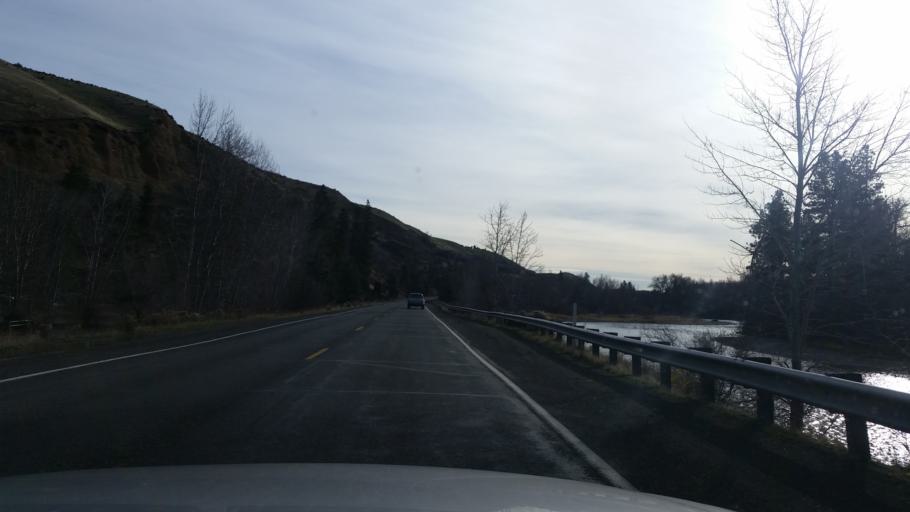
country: US
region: Washington
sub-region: Kittitas County
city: Ellensburg
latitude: 47.0760
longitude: -120.6646
